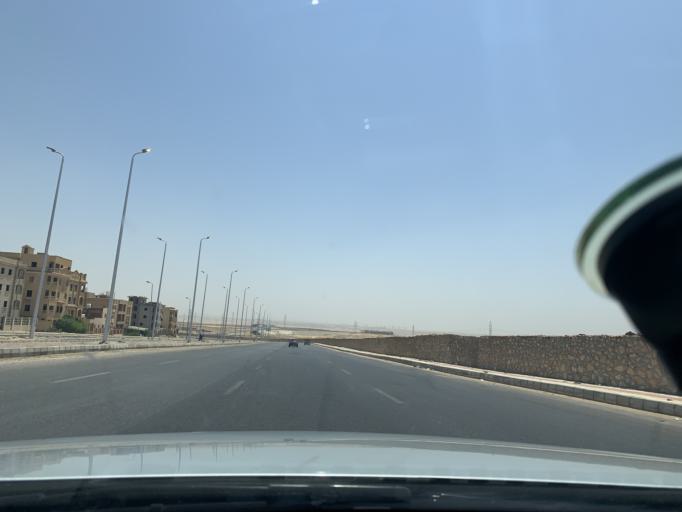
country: EG
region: Muhafazat al Qahirah
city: Halwan
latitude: 29.9816
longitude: 31.4686
